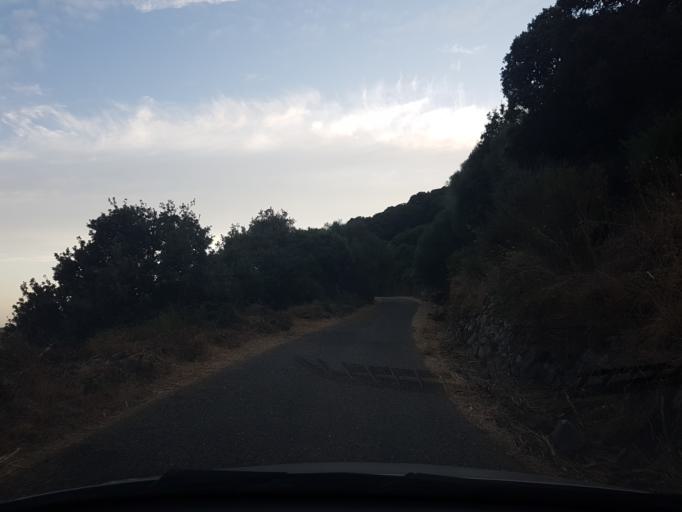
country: IT
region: Sardinia
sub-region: Provincia di Oristano
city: Seneghe
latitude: 40.1087
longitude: 8.6049
